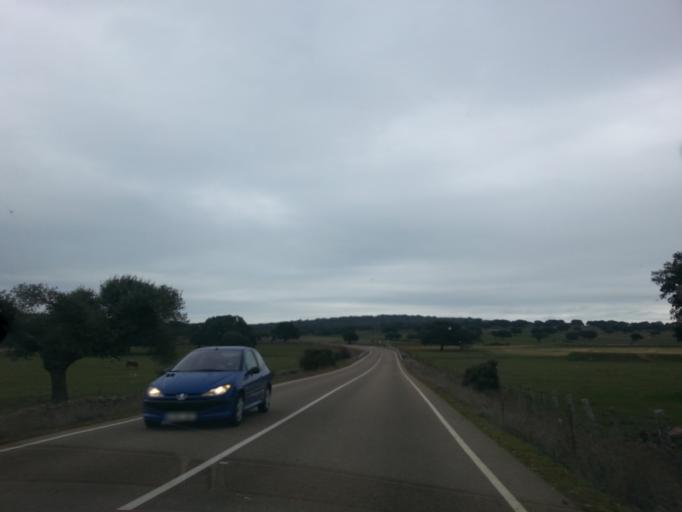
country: ES
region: Castille and Leon
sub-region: Provincia de Salamanca
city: Berrocal de Huebra
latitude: 40.7205
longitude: -5.9693
